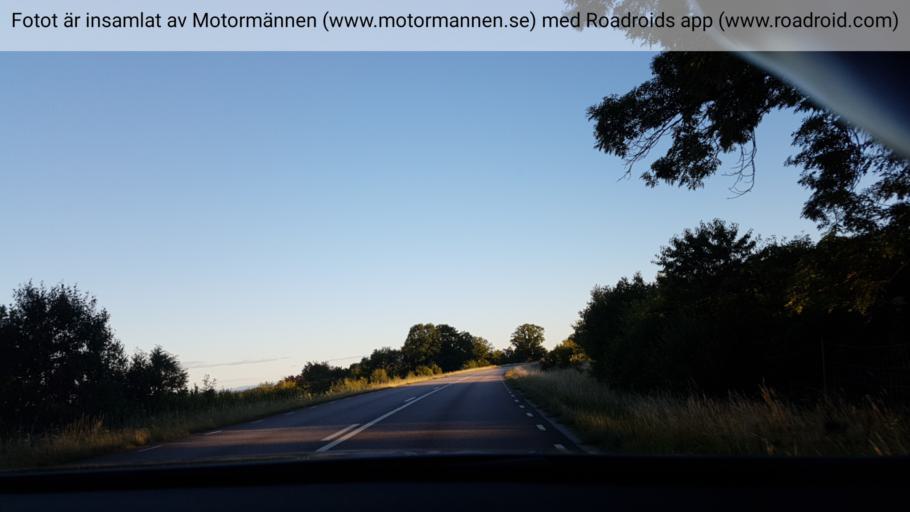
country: SE
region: Vaestra Goetaland
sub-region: Hjo Kommun
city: Hjo
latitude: 58.3357
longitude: 14.3366
